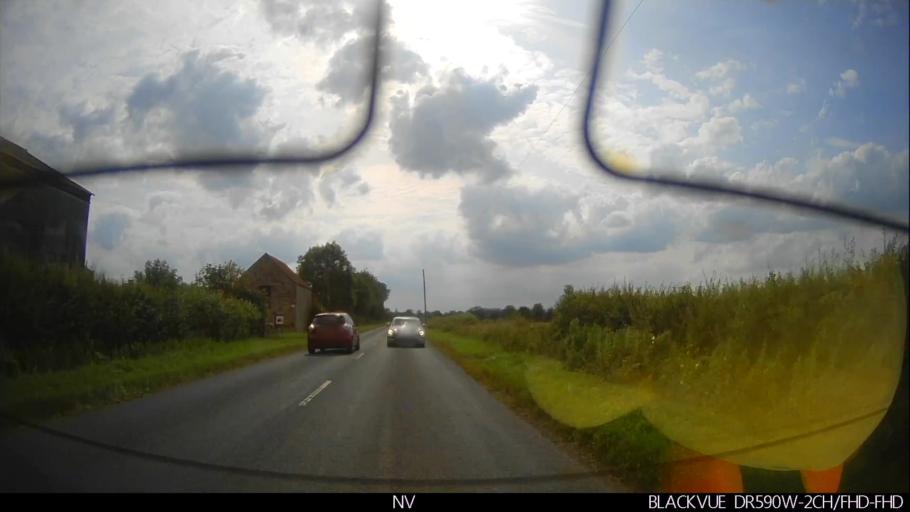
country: GB
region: England
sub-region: North Yorkshire
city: Marishes
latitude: 54.2088
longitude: -0.7861
